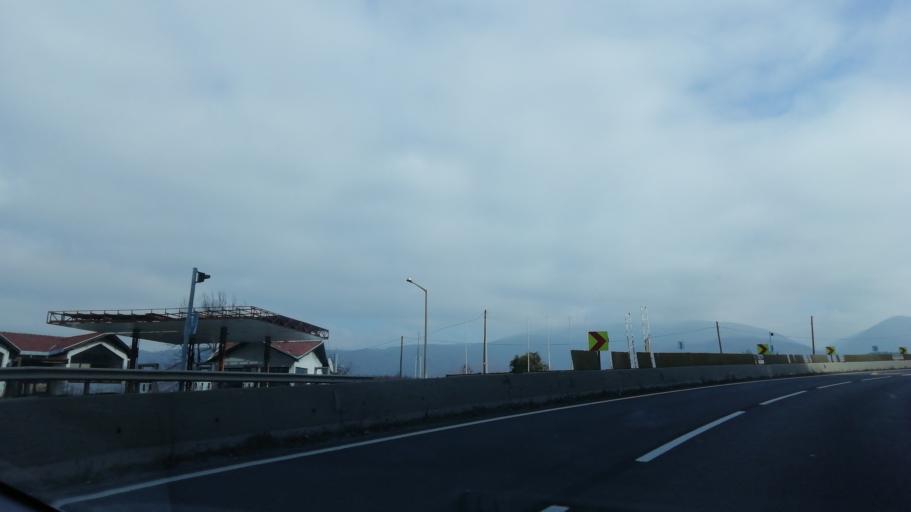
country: TR
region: Duzce
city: Kaynasli
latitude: 40.7574
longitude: 31.3670
